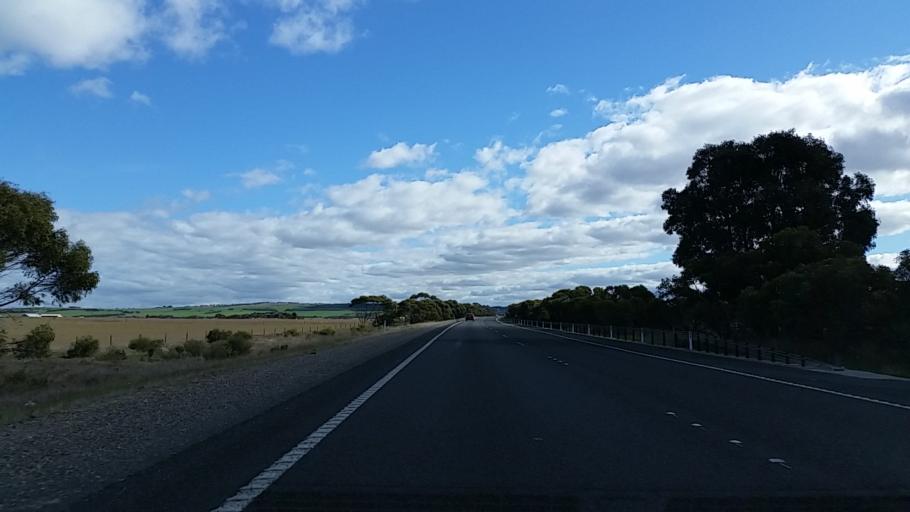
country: AU
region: South Australia
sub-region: Murray Bridge
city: Murray Bridge
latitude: -35.1506
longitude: 139.2722
